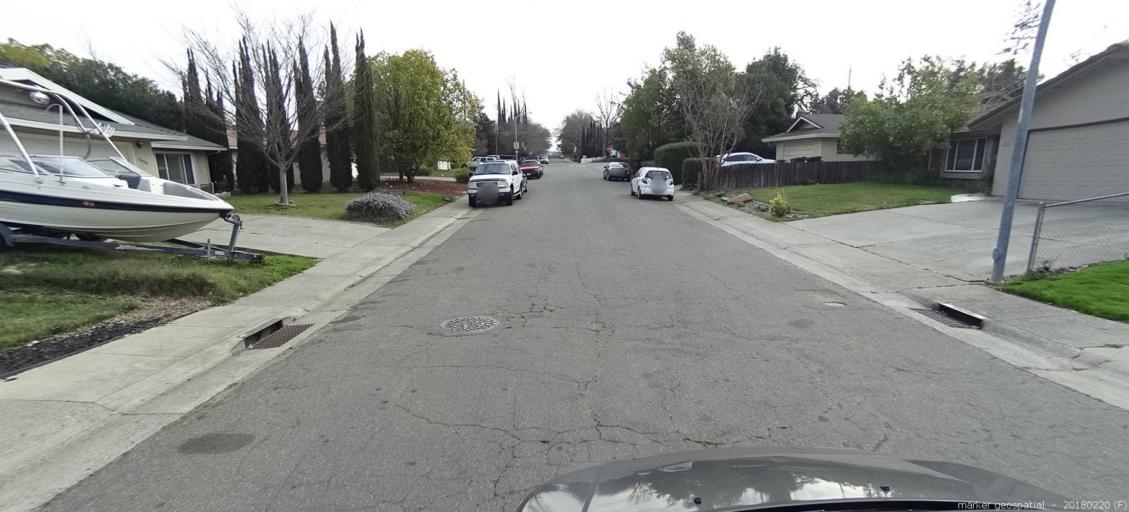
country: US
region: California
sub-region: Sacramento County
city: Orangevale
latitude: 38.6699
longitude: -121.2270
